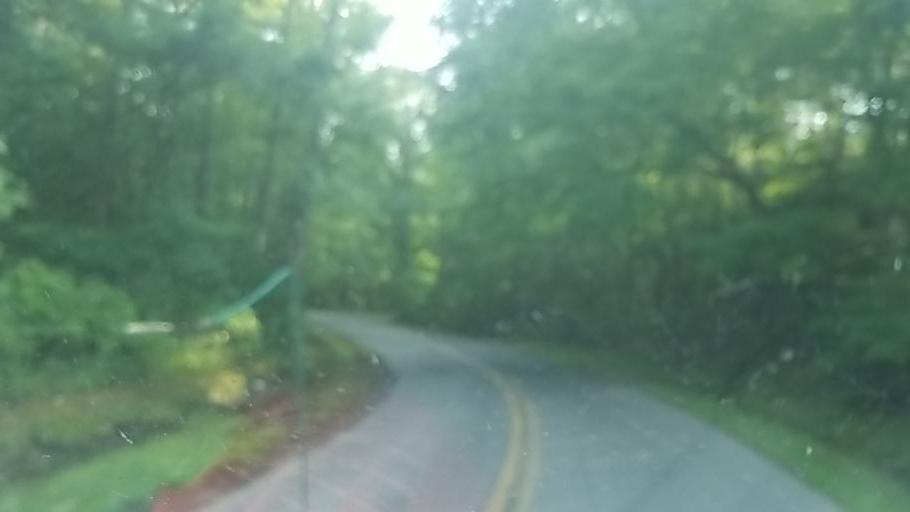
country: US
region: Maryland
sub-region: Worcester County
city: West Ocean City
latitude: 38.3149
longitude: -75.1463
